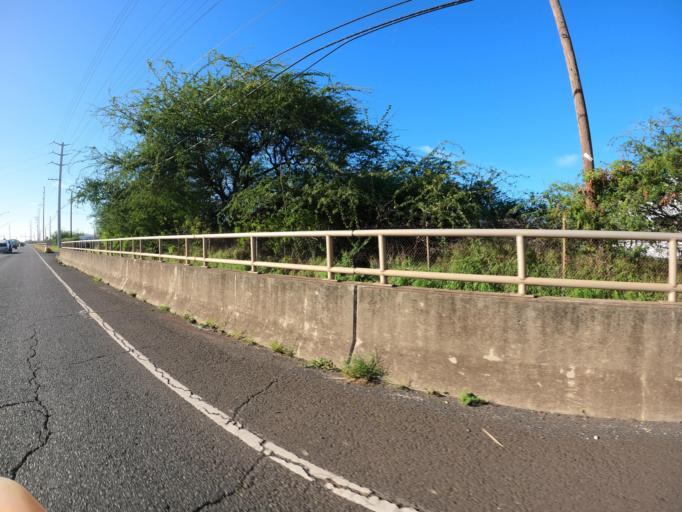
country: US
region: Hawaii
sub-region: Honolulu County
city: Honolulu
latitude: 21.3114
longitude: -157.8868
